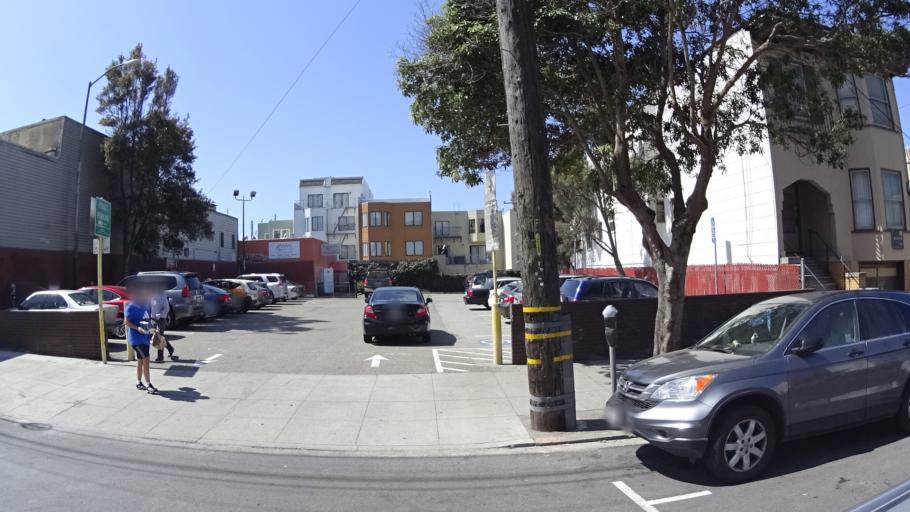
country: US
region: California
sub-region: San Francisco County
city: San Francisco
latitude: 37.7640
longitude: -122.4783
